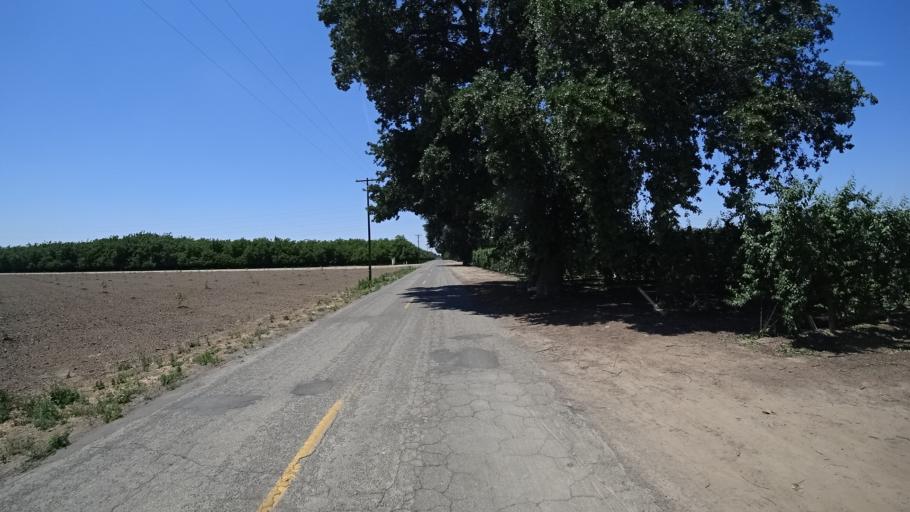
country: US
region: California
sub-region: Kings County
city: Lucerne
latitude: 36.4303
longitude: -119.5905
